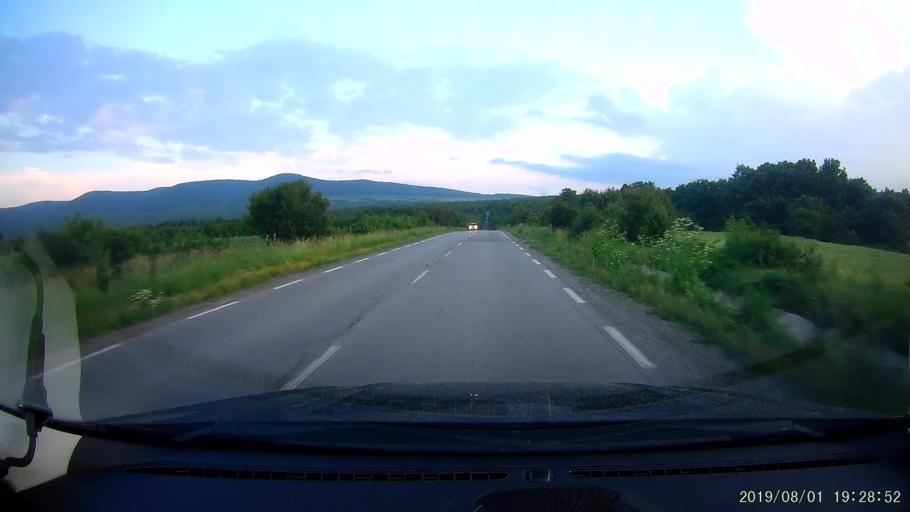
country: BG
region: Burgas
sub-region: Obshtina Sungurlare
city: Sungurlare
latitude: 42.8357
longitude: 26.9126
